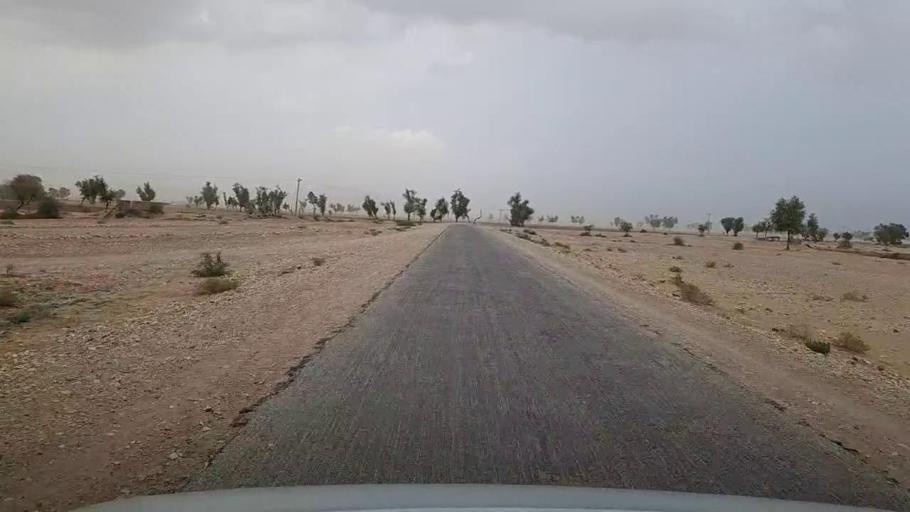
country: PK
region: Sindh
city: Sehwan
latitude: 26.3193
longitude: 67.7296
